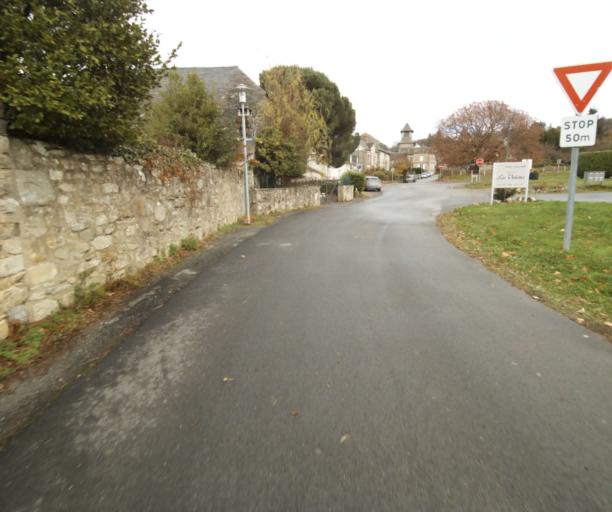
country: FR
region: Limousin
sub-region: Departement de la Correze
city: Saint-Mexant
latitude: 45.2734
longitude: 1.6323
